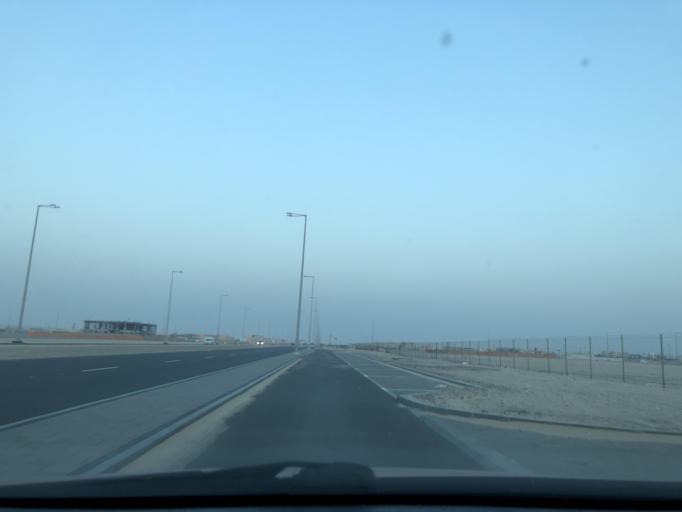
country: AE
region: Abu Dhabi
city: Abu Dhabi
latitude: 24.3606
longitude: 54.6060
